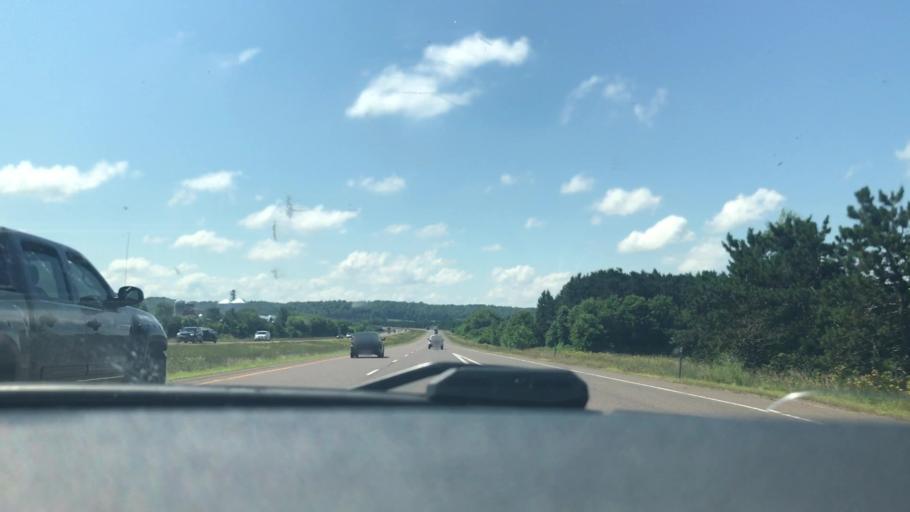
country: US
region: Wisconsin
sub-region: Chippewa County
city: Chippewa Falls
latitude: 44.9961
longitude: -91.4425
